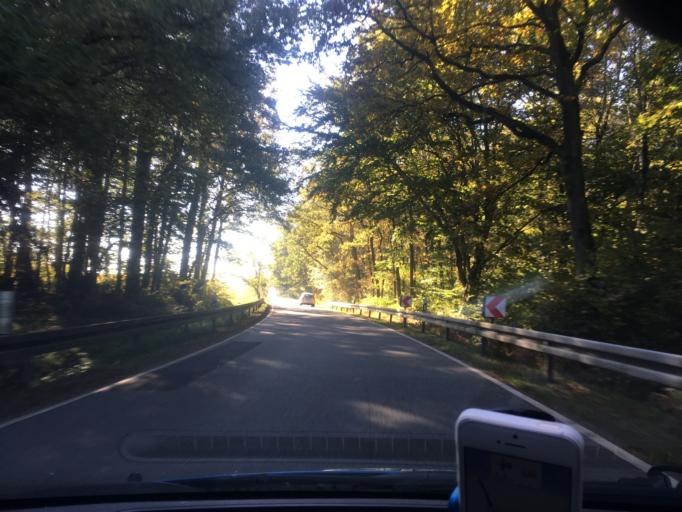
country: DE
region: Mecklenburg-Vorpommern
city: Dummer
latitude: 53.5456
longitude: 11.1502
